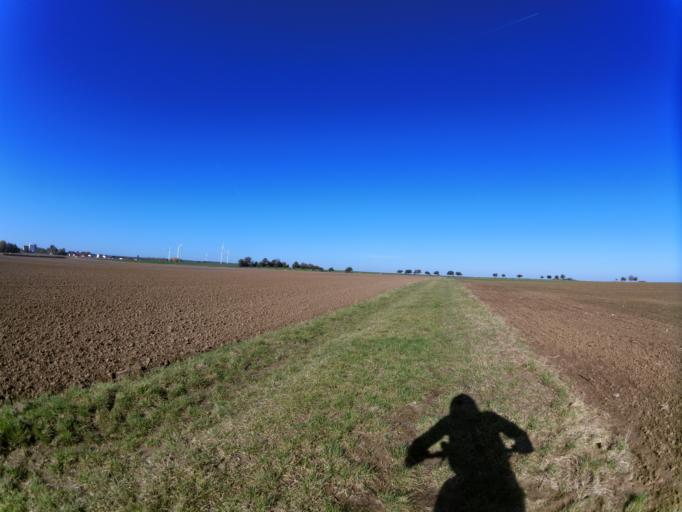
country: DE
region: Bavaria
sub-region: Regierungsbezirk Unterfranken
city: Geroldshausen
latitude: 49.6856
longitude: 9.9173
